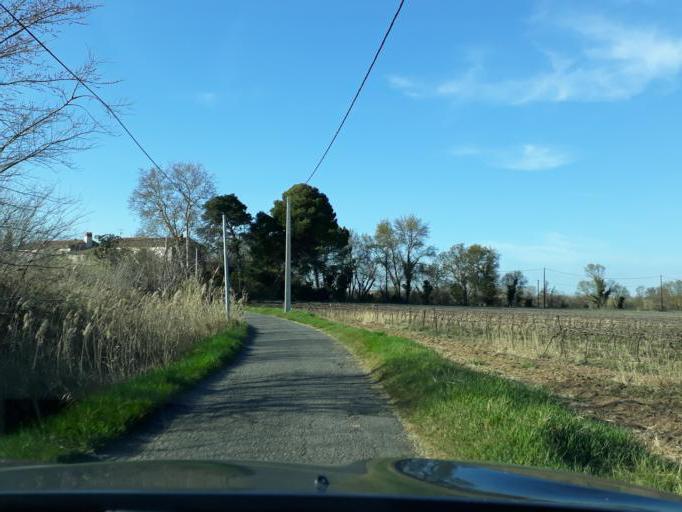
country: FR
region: Languedoc-Roussillon
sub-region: Departement de l'Herault
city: Agde
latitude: 43.3267
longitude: 3.4522
